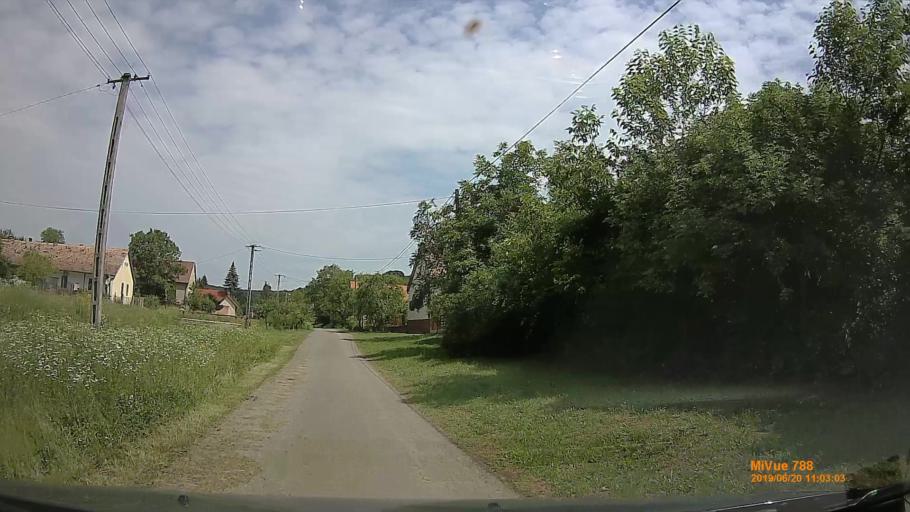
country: HU
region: Baranya
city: Mecseknadasd
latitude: 46.1803
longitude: 18.5121
